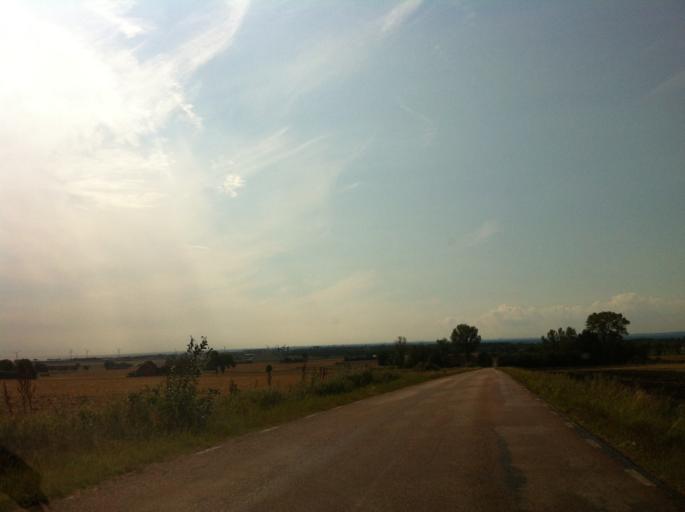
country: SE
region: Skane
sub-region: Helsingborg
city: Glumslov
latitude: 55.9231
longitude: 12.8720
